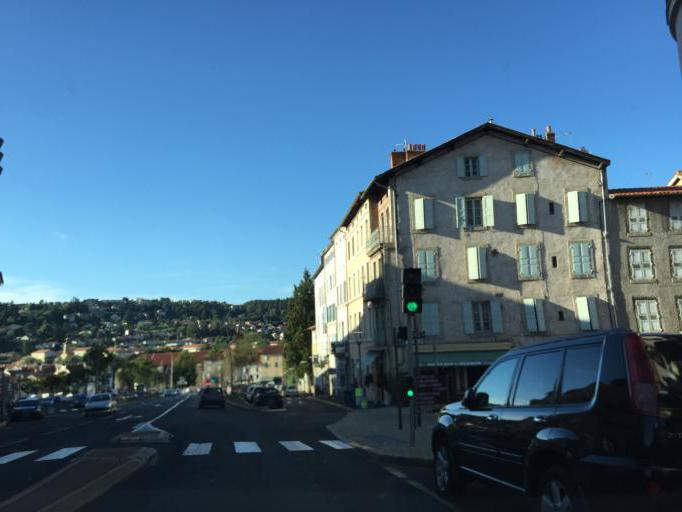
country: FR
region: Auvergne
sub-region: Departement de la Haute-Loire
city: Le Puy-en-Velay
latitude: 45.0450
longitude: 3.8801
